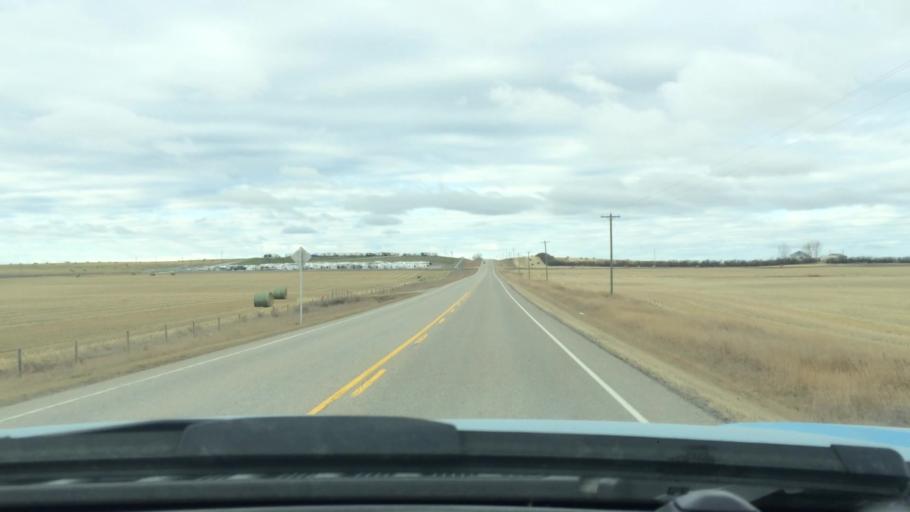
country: CA
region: Alberta
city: Airdrie
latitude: 51.2126
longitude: -114.0409
